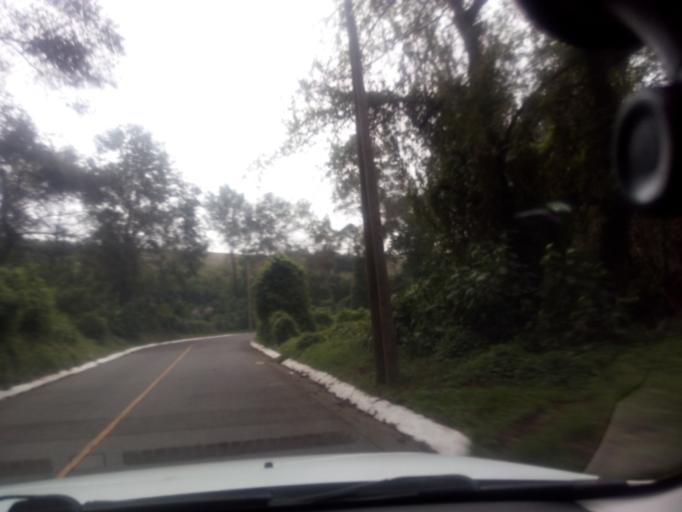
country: GT
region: Sacatepequez
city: San Bartolome Milpas Altas
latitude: 14.5972
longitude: -90.6845
